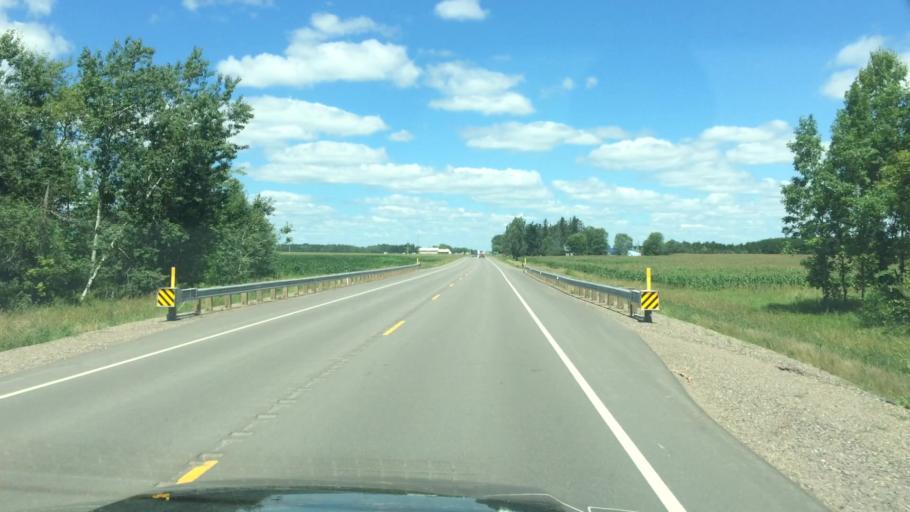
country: US
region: Wisconsin
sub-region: Clark County
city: Abbotsford
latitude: 45.0286
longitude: -90.3150
